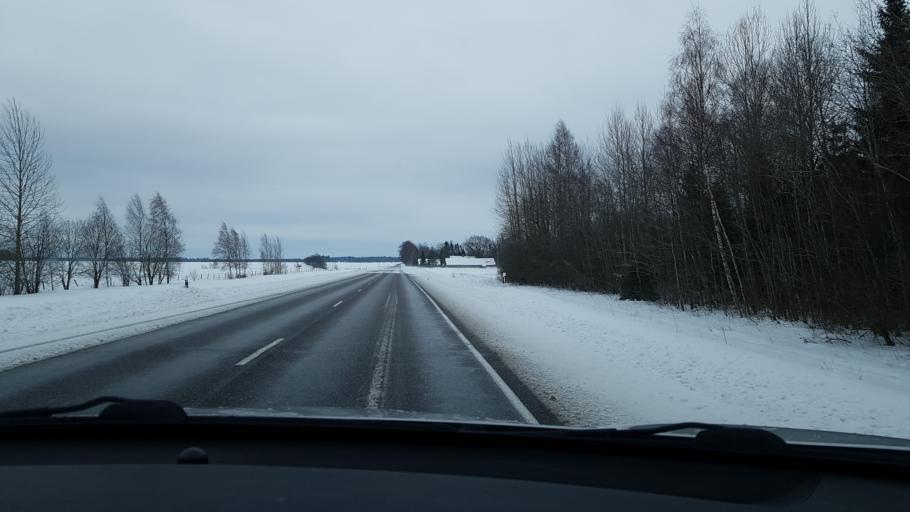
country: EE
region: Jaervamaa
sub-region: Jaerva-Jaani vald
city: Jarva-Jaani
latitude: 59.1259
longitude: 25.7837
